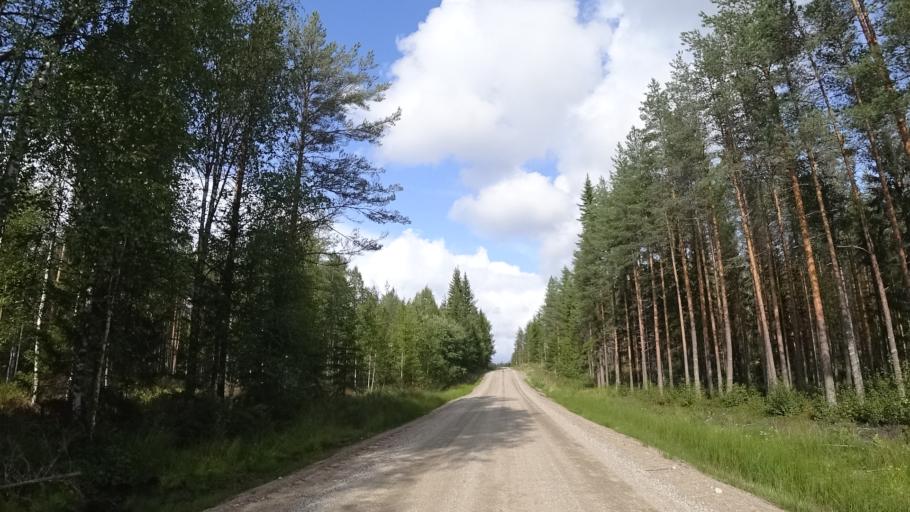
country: FI
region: North Karelia
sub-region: Pielisen Karjala
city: Lieksa
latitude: 63.5918
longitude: 30.1361
